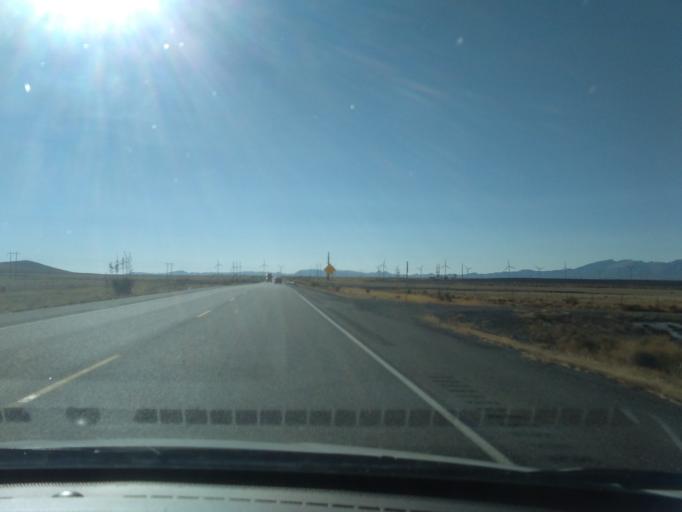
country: US
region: New Mexico
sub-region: Dona Ana County
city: Hatch
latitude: 32.5683
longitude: -107.4604
